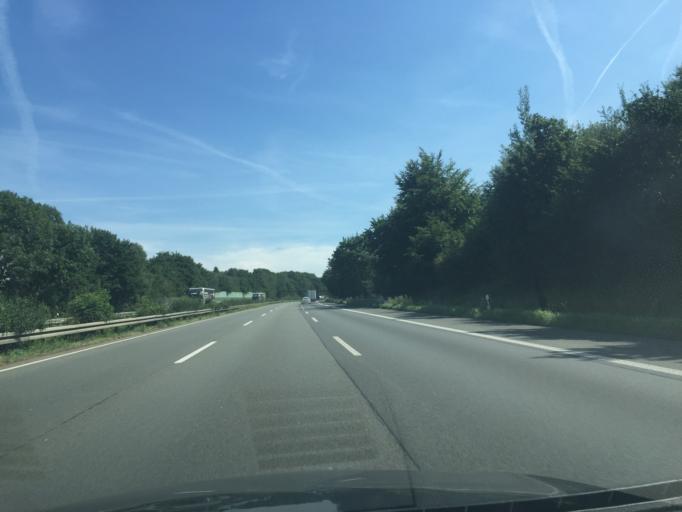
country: DE
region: North Rhine-Westphalia
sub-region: Regierungsbezirk Arnsberg
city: Nachrodt-Wiblingwerde
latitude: 51.2776
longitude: 7.5930
